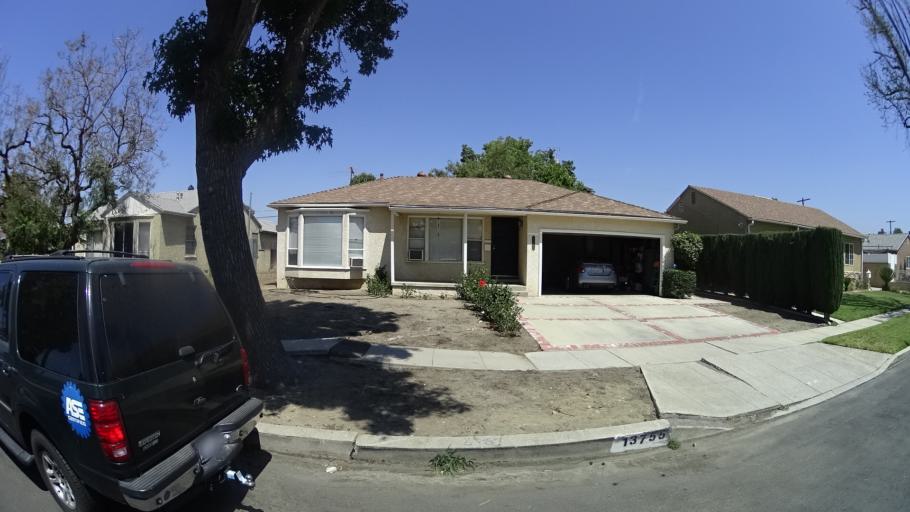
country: US
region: California
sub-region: Los Angeles County
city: Van Nuys
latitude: 34.2282
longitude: -118.4323
